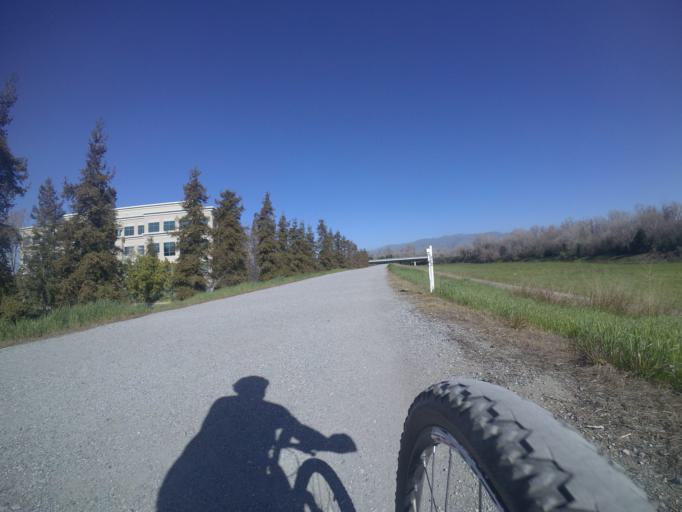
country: US
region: California
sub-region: Santa Clara County
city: Milpitas
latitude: 37.4083
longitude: -121.9255
